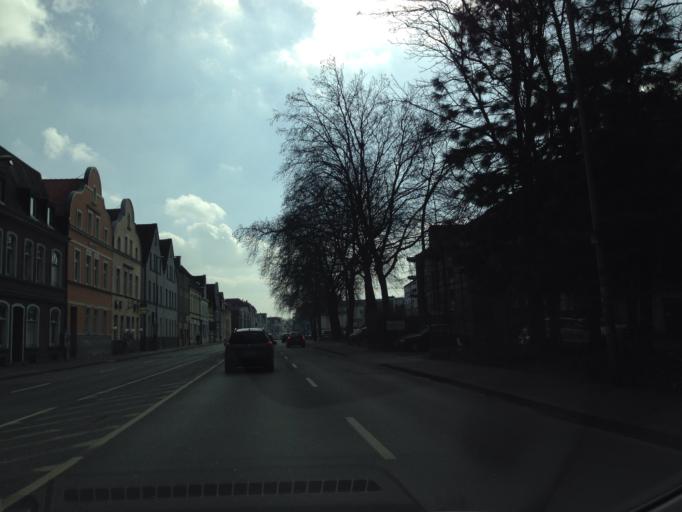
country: DE
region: North Rhine-Westphalia
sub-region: Regierungsbezirk Munster
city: Muenster
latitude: 51.9733
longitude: 7.6125
